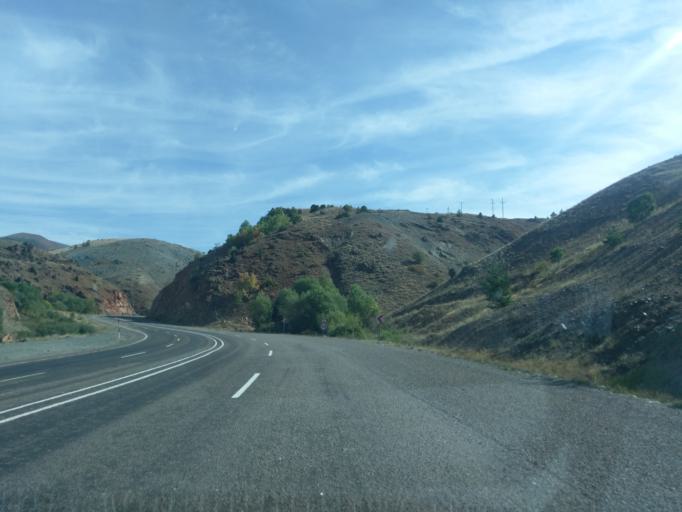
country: TR
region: Sivas
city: Imranli
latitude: 39.8576
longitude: 38.3151
